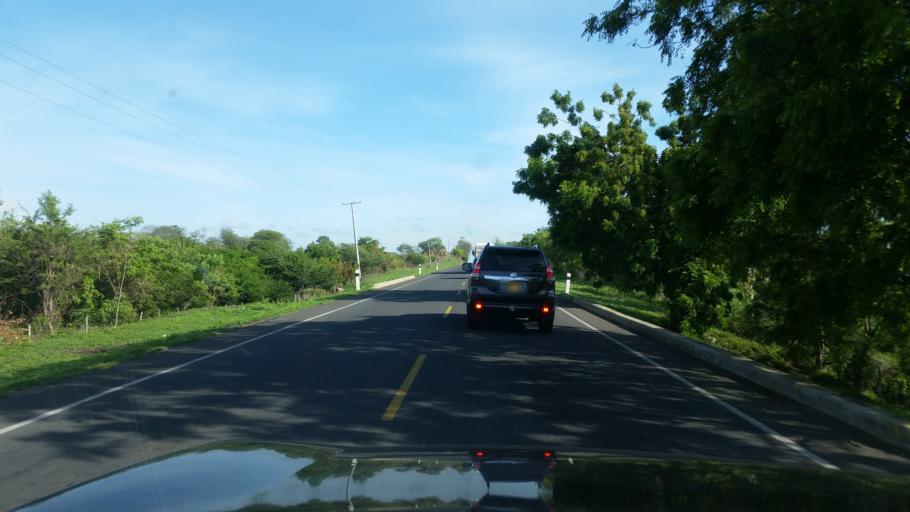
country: NI
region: Leon
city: La Paz Centro
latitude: 12.2250
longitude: -86.6971
